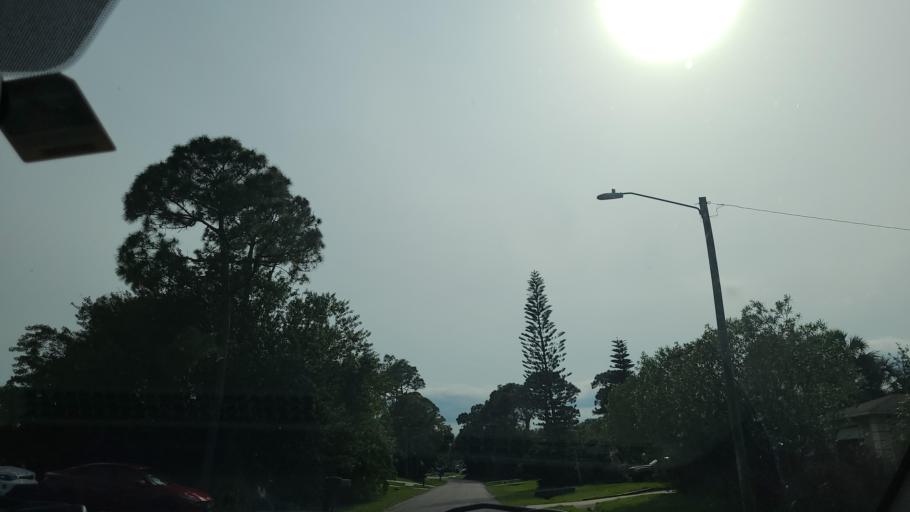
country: US
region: Florida
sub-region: Indian River County
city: Sebastian
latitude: 27.7629
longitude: -80.4770
